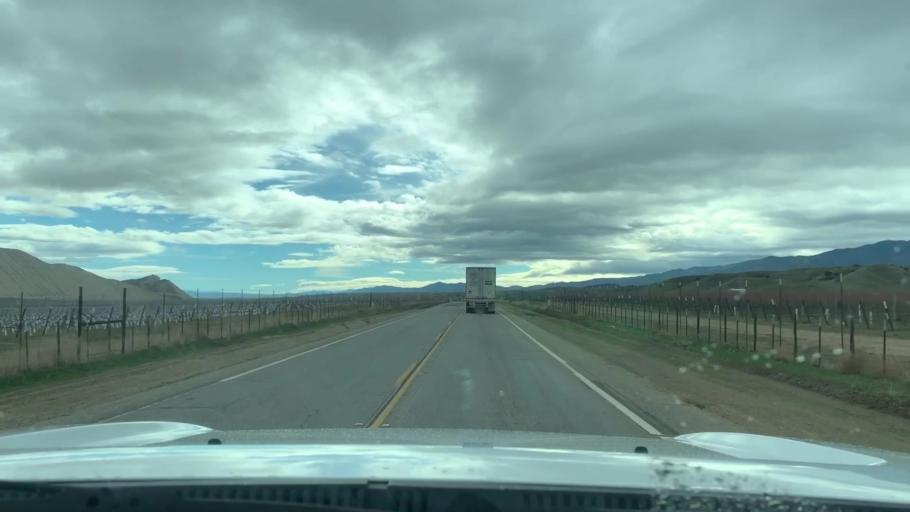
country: US
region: California
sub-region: Kern County
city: Taft Heights
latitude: 35.0243
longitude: -119.8614
